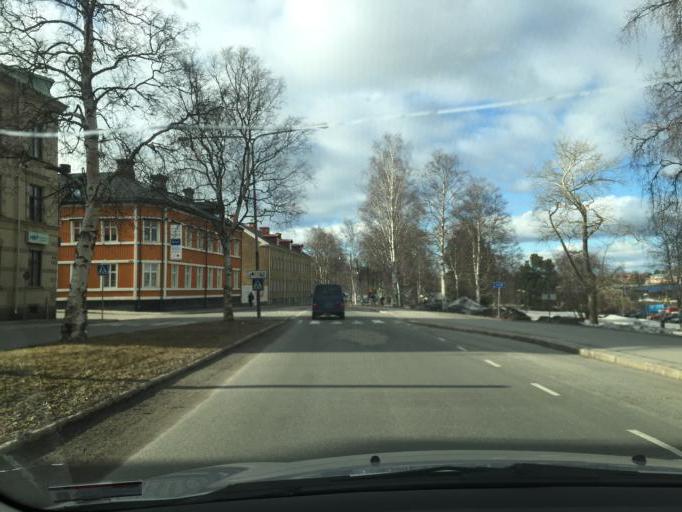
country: SE
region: Norrbotten
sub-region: Lulea Kommun
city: Lulea
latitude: 65.5836
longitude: 22.1638
